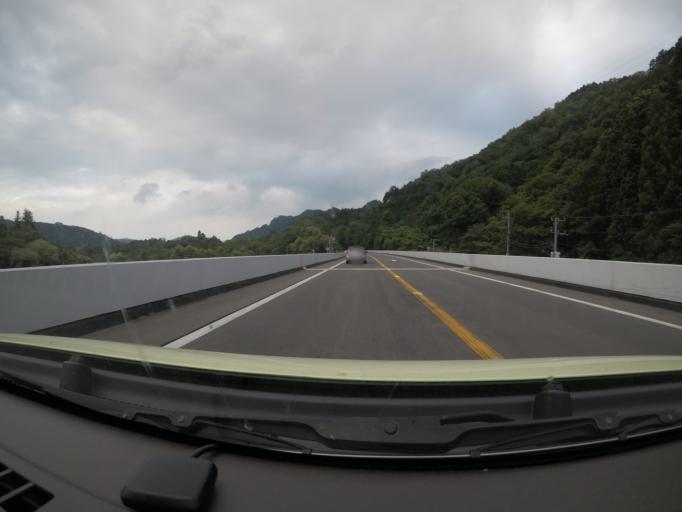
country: JP
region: Tochigi
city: Nikko
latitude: 36.7471
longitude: 139.5782
